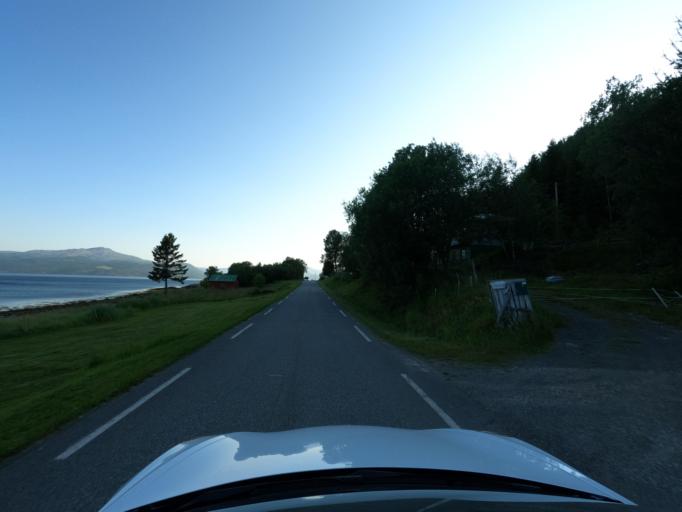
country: NO
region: Nordland
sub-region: Ballangen
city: Ballangen
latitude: 68.4662
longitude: 16.7830
